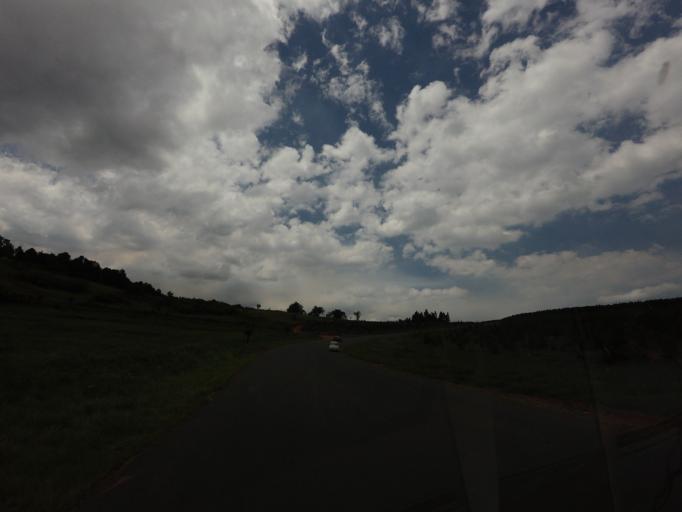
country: ZA
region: Mpumalanga
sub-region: Ehlanzeni District
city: Graksop
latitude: -24.9855
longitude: 30.8125
